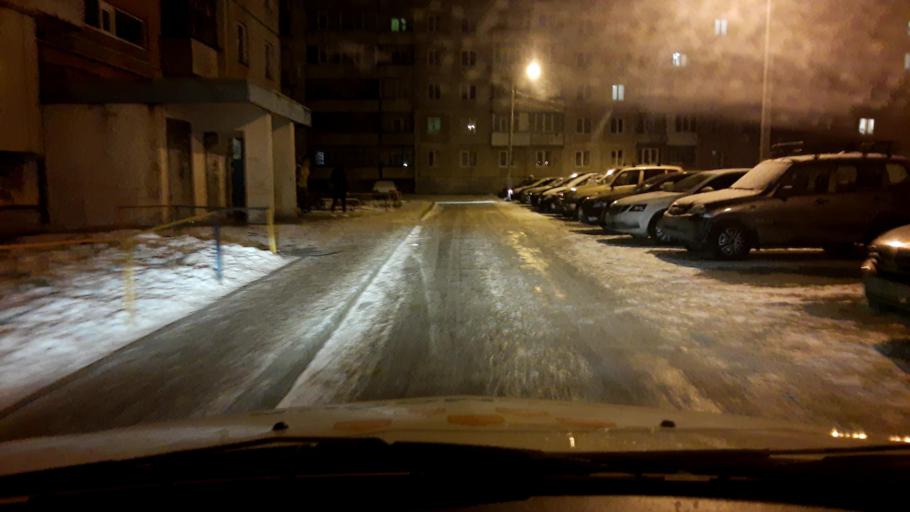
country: RU
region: Bashkortostan
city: Iglino
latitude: 54.7695
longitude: 56.2232
